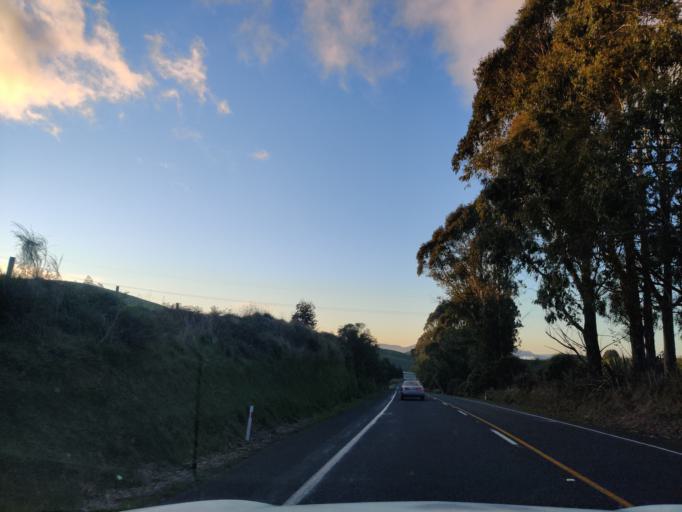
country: NZ
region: Waikato
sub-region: Taupo District
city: Taupo
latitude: -38.6272
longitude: 176.0402
